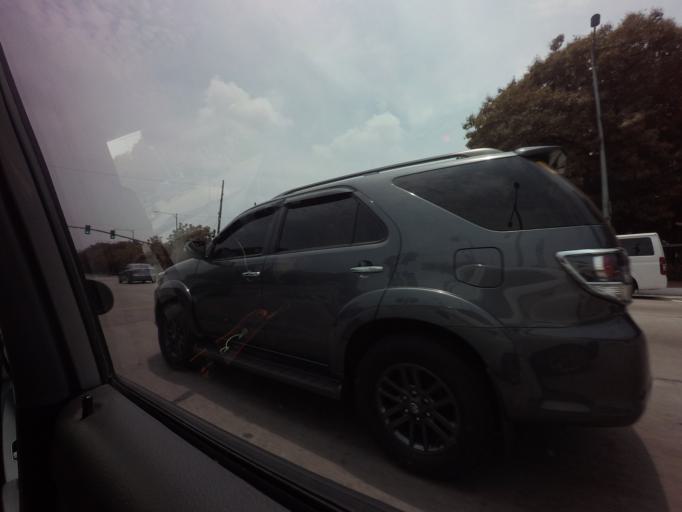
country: PH
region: Metro Manila
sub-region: City of Manila
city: Port Area
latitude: 14.5827
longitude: 120.9756
